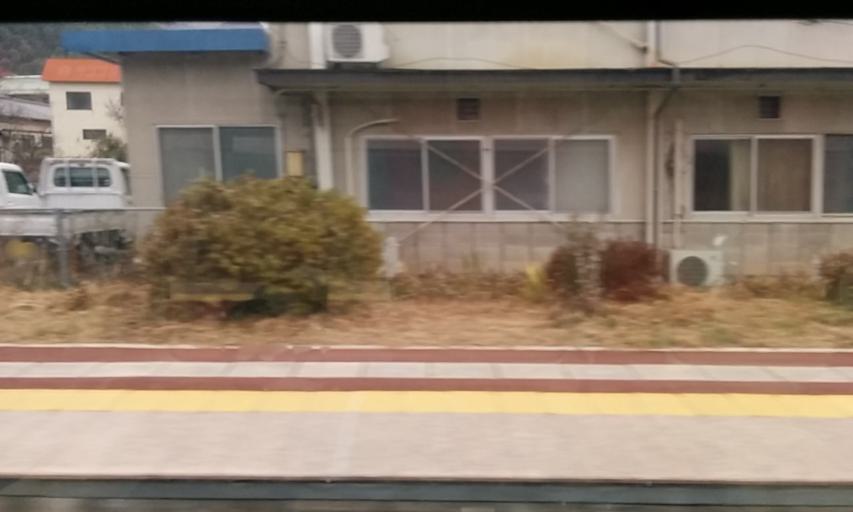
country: JP
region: Nagano
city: Omachi
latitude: 36.4550
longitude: 138.0471
